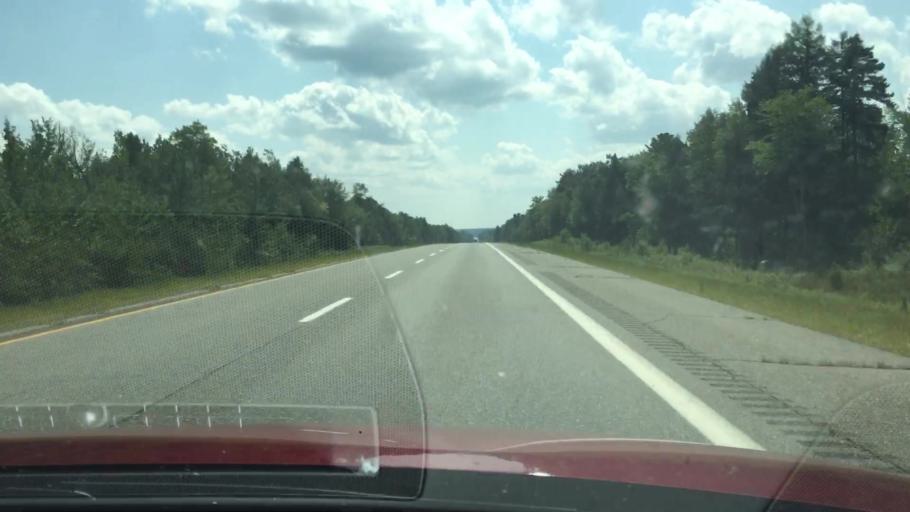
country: US
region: Maine
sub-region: Penobscot County
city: Lincoln
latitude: 45.4191
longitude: -68.5920
